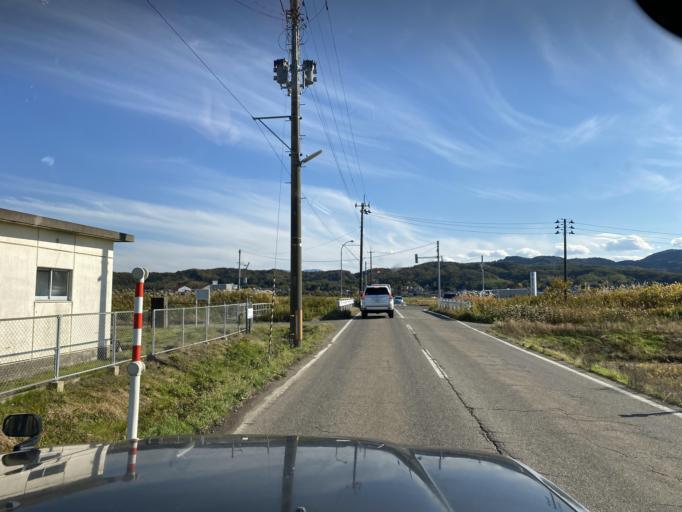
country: JP
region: Niigata
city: Niitsu-honcho
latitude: 37.7567
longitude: 139.0909
